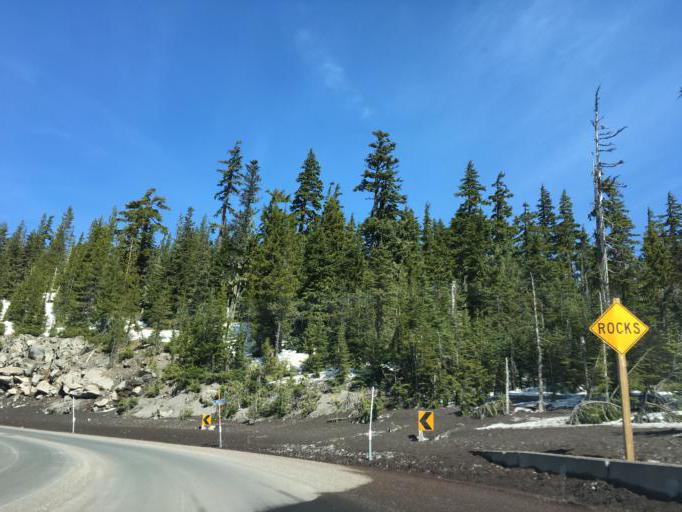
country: US
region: Oregon
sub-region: Clackamas County
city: Mount Hood Village
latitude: 45.3067
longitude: -121.7016
